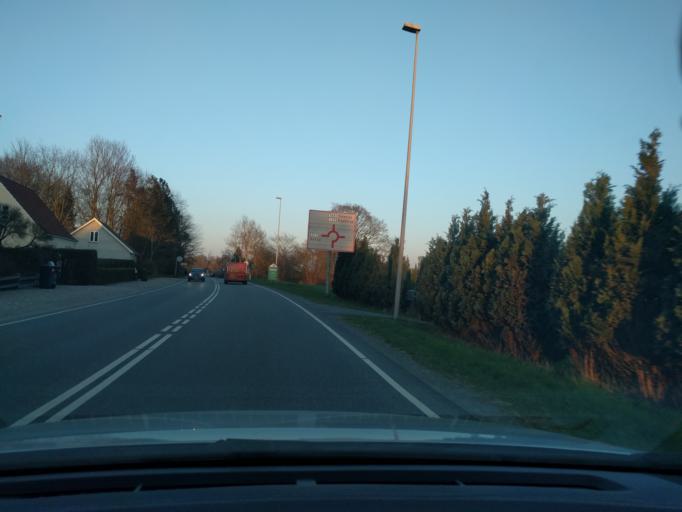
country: DK
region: South Denmark
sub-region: Assens Kommune
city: Glamsbjerg
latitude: 55.2690
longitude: 10.1033
